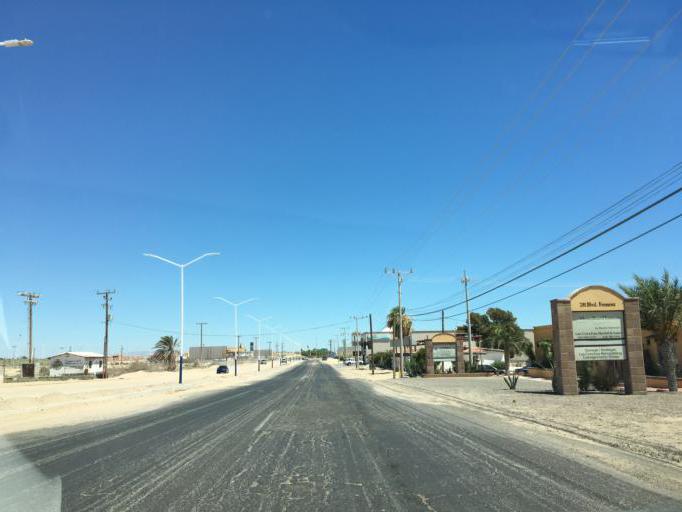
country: MX
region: Sonora
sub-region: Puerto Penasco
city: Puerto Penasco
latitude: 31.3058
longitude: -113.5242
